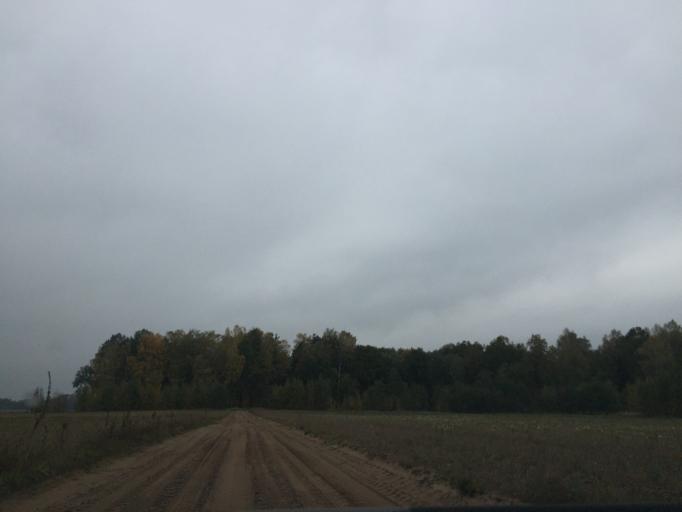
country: LV
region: Dobeles Rajons
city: Dobele
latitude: 56.6730
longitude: 23.4483
